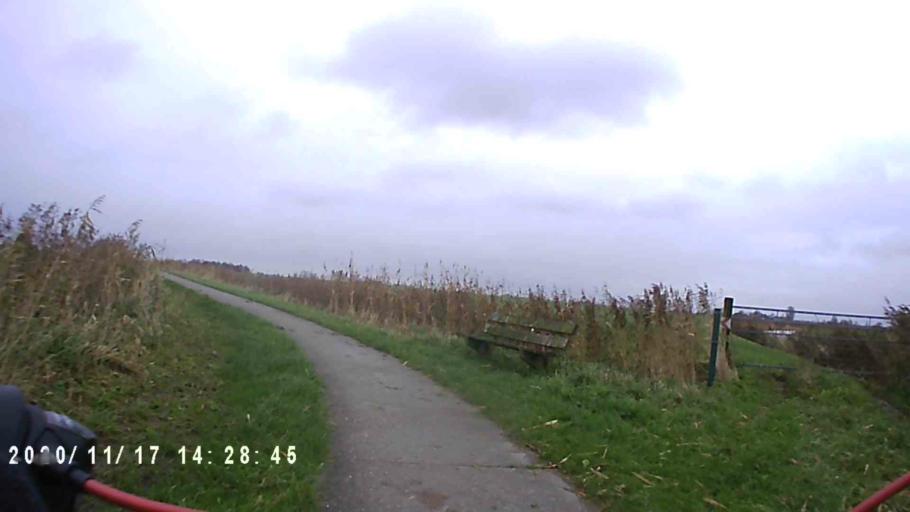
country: NL
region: Groningen
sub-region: Gemeente Zuidhorn
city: Grijpskerk
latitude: 53.2722
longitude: 6.3498
